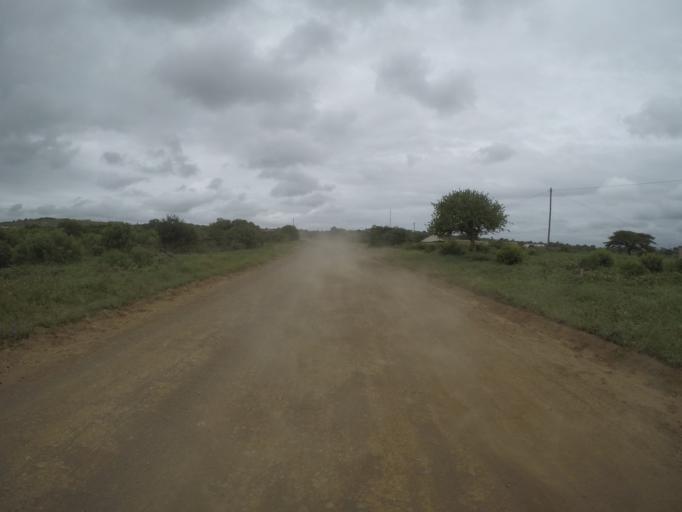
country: ZA
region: KwaZulu-Natal
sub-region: uThungulu District Municipality
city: Empangeni
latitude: -28.5974
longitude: 31.8381
